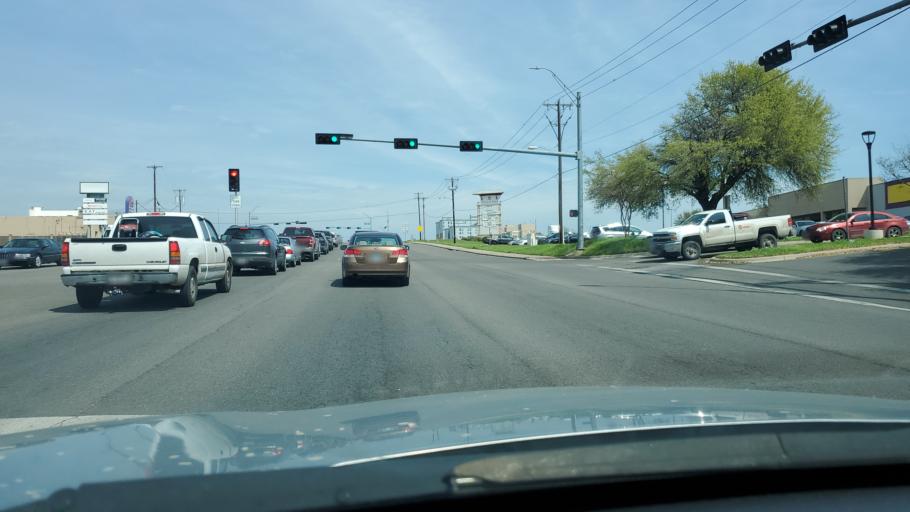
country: US
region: Texas
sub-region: Bell County
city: Temple
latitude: 31.0706
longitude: -97.3689
